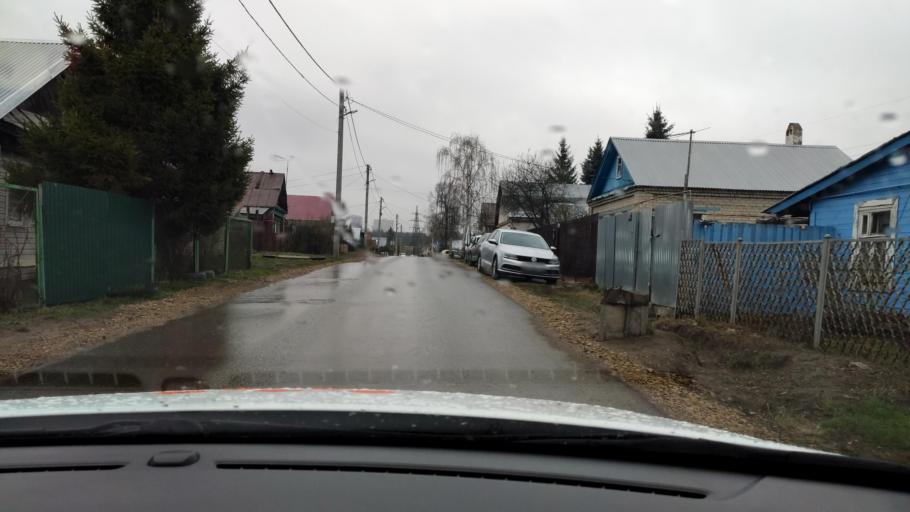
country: RU
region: Tatarstan
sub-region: Gorod Kazan'
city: Kazan
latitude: 55.7251
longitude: 49.1457
